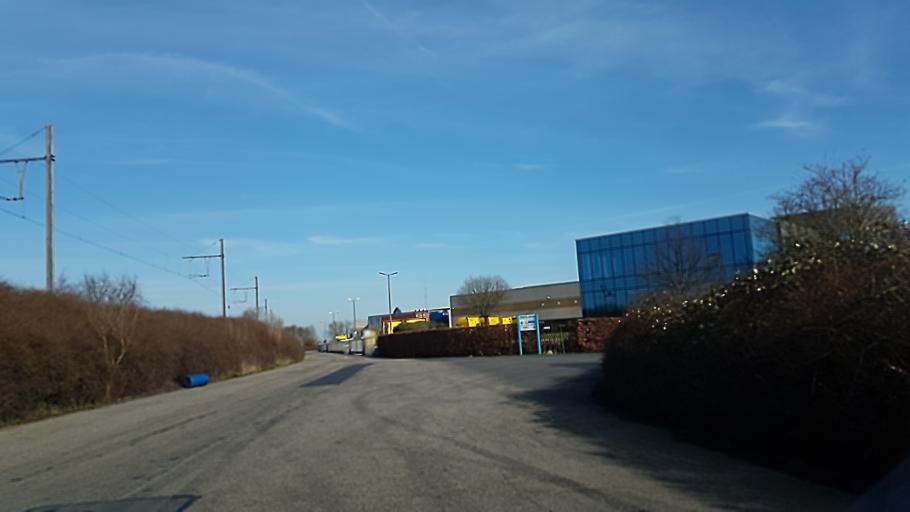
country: BE
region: Flanders
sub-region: Provincie Antwerpen
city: Stabroek
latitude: 51.2966
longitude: 4.3471
